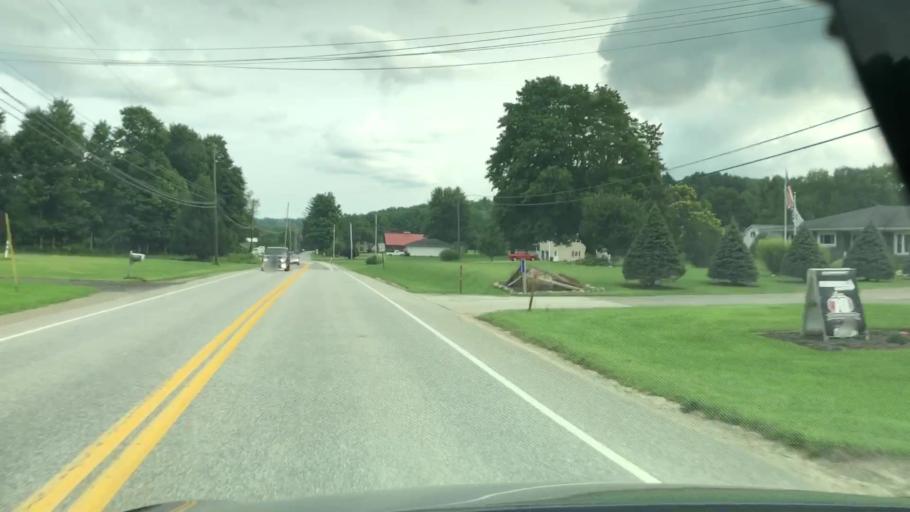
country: US
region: Pennsylvania
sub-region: Erie County
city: Union City
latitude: 42.0090
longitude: -79.8147
